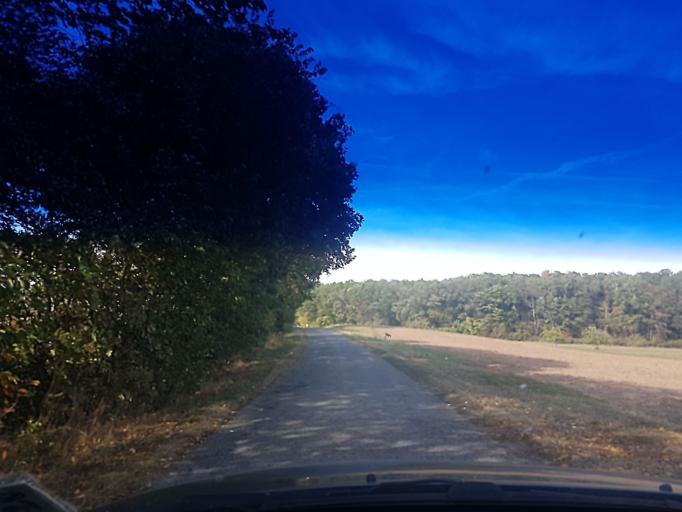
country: DE
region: Bavaria
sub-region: Regierungsbezirk Mittelfranken
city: Burghaslach
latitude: 49.7698
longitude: 10.5434
